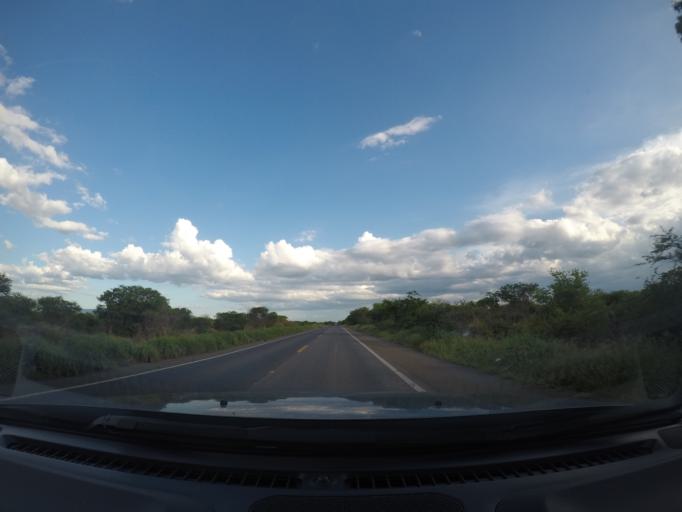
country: BR
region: Bahia
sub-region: Oliveira Dos Brejinhos
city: Beira Rio
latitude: -12.2128
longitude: -42.8002
